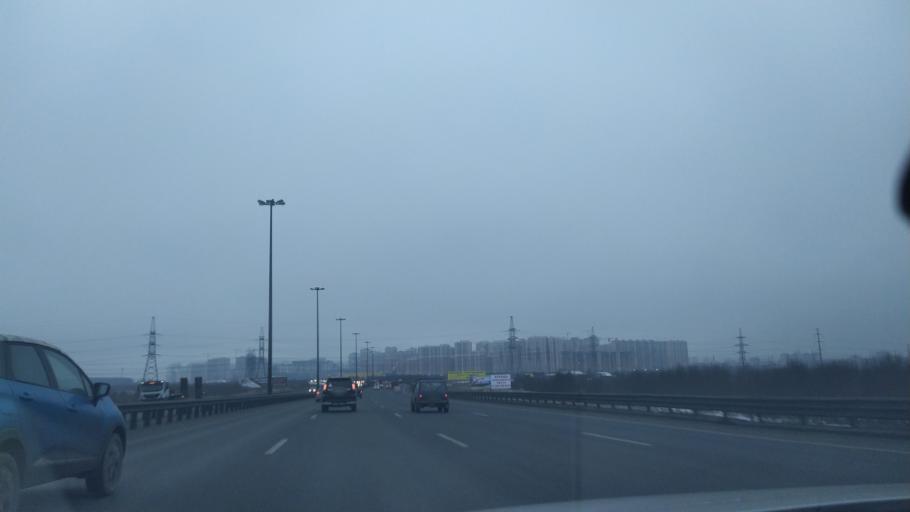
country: RU
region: St.-Petersburg
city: Krasnogvargeisky
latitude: 59.9284
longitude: 30.5339
